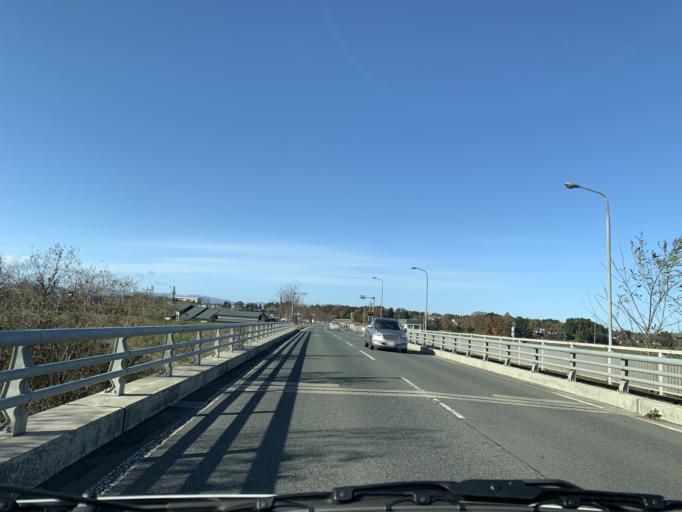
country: JP
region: Iwate
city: Mizusawa
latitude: 39.1874
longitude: 141.1263
